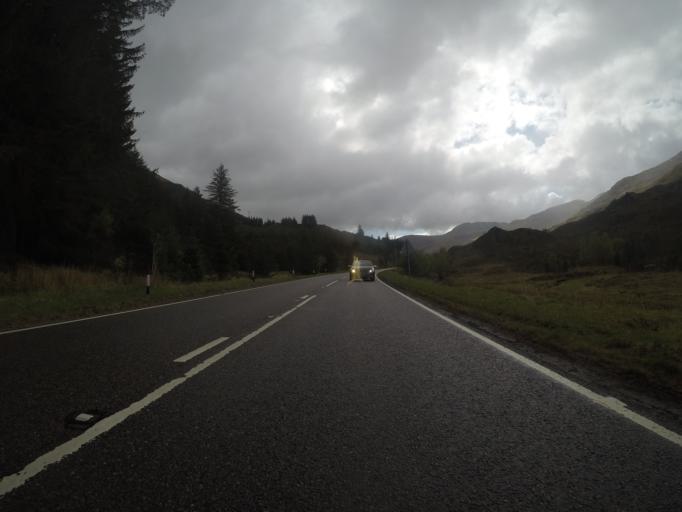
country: GB
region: Scotland
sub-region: Highland
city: Fort William
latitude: 57.1639
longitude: -5.2732
